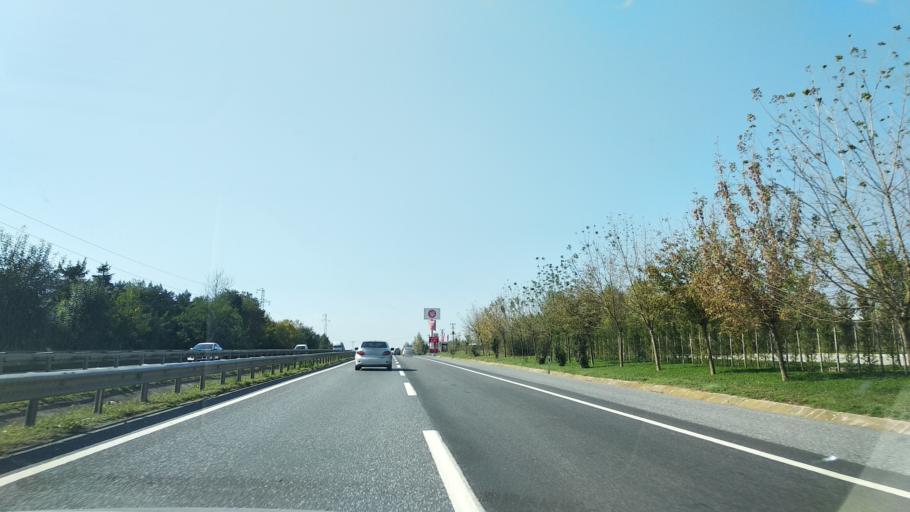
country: TR
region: Kocaeli
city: Derbent
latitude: 40.7313
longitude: 30.1624
